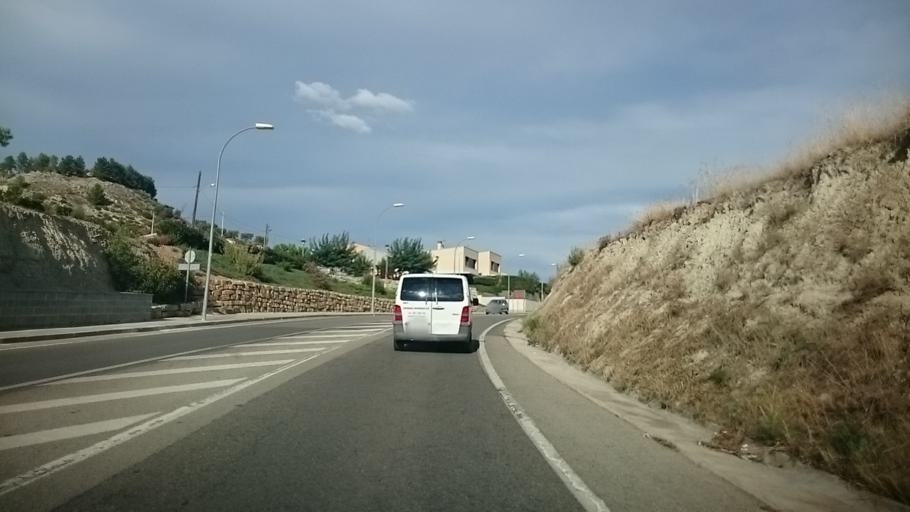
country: ES
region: Catalonia
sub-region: Provincia de Barcelona
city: Odena
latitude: 41.6022
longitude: 1.6367
